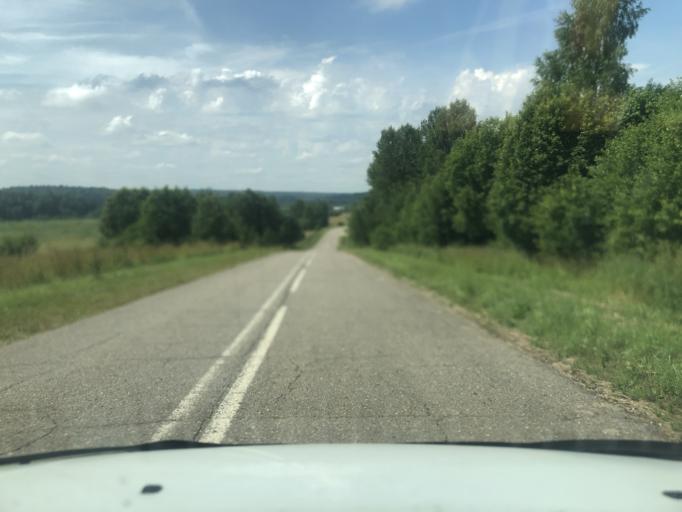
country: RU
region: Jaroslavl
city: Pereslavl'-Zalesskiy
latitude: 57.0405
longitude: 38.8769
